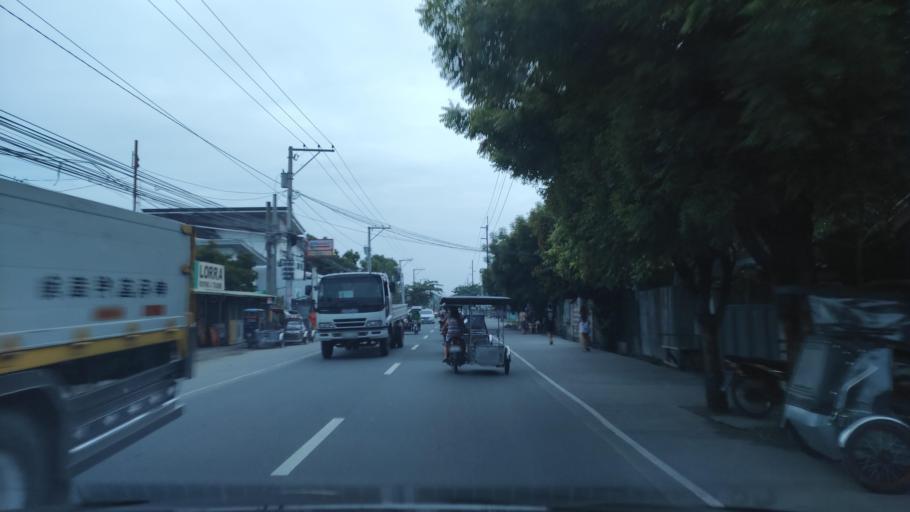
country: PH
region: Central Luzon
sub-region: Province of Pampanga
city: Santa Ana
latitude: 15.1063
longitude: 120.7713
